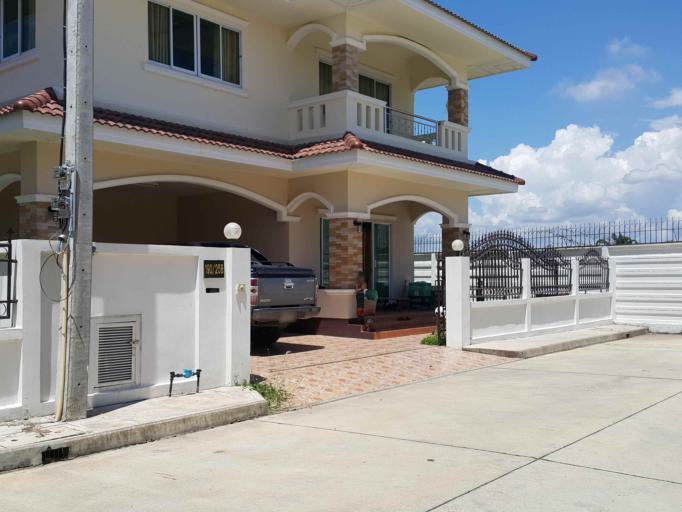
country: TH
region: Chiang Mai
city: San Kamphaeng
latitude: 18.7561
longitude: 99.0711
